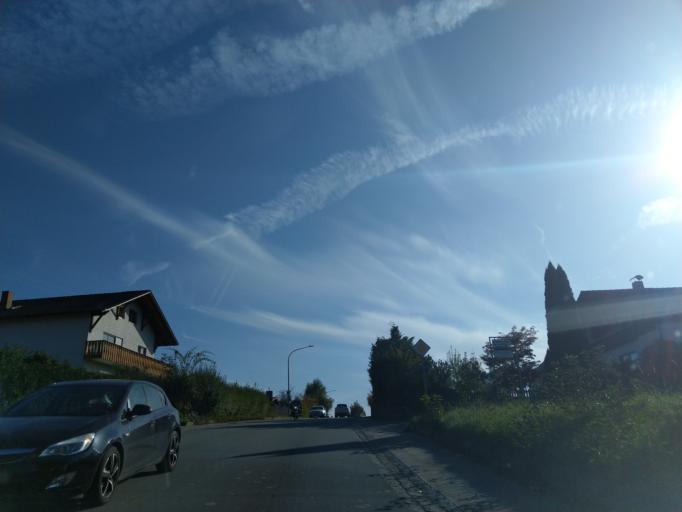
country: DE
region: Bavaria
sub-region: Lower Bavaria
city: Metten
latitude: 48.8919
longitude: 12.9251
